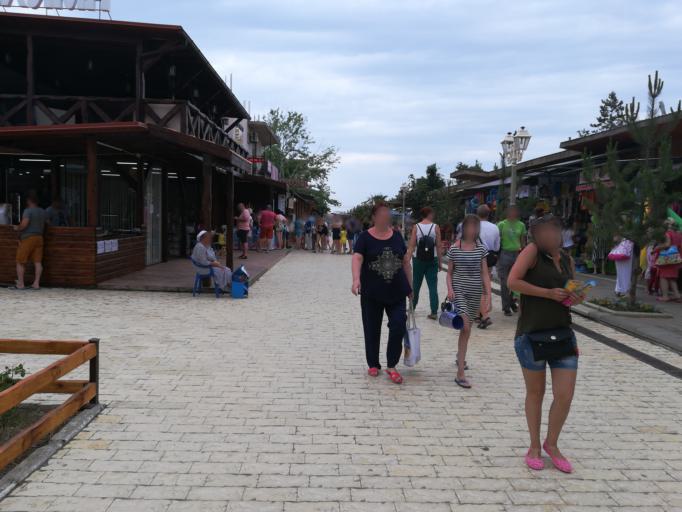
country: RU
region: Krasnodarskiy
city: Vityazevo
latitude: 44.9847
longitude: 37.2530
